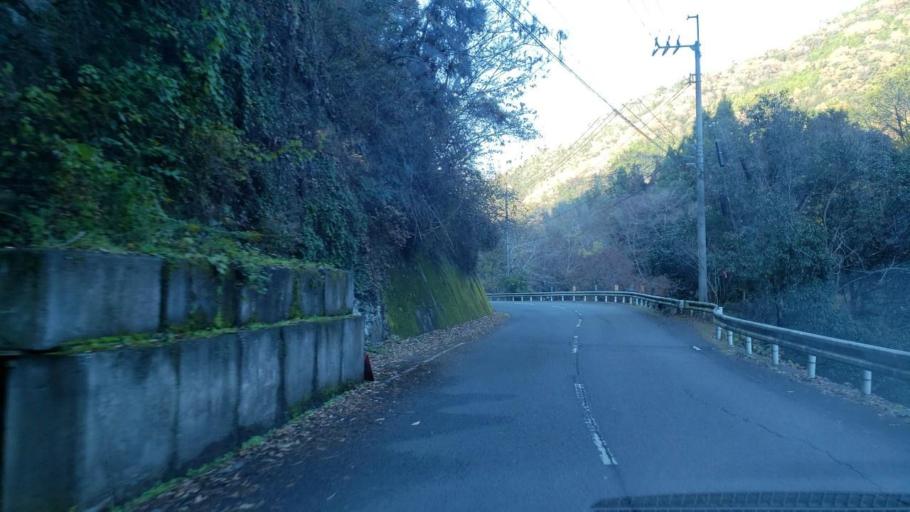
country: JP
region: Tokushima
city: Wakimachi
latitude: 34.0027
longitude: 134.0357
